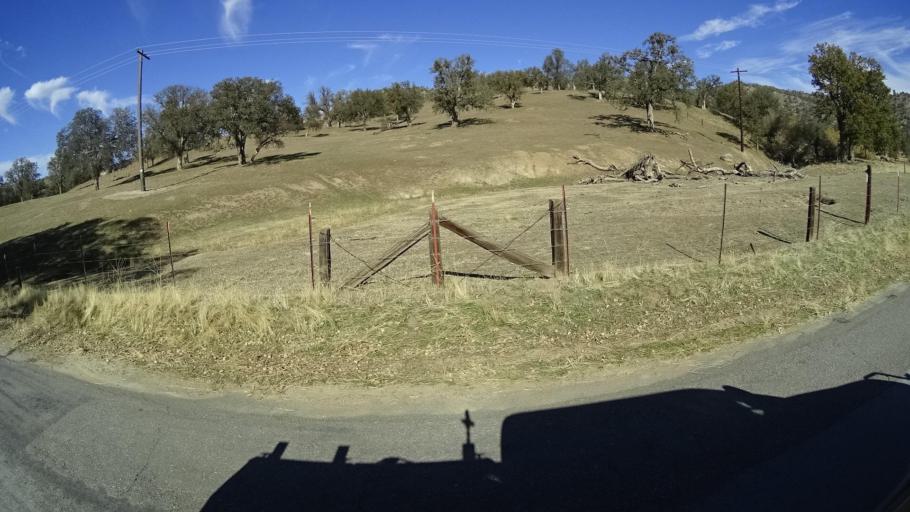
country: US
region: California
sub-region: Kern County
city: Alta Sierra
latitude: 35.6183
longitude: -118.7293
